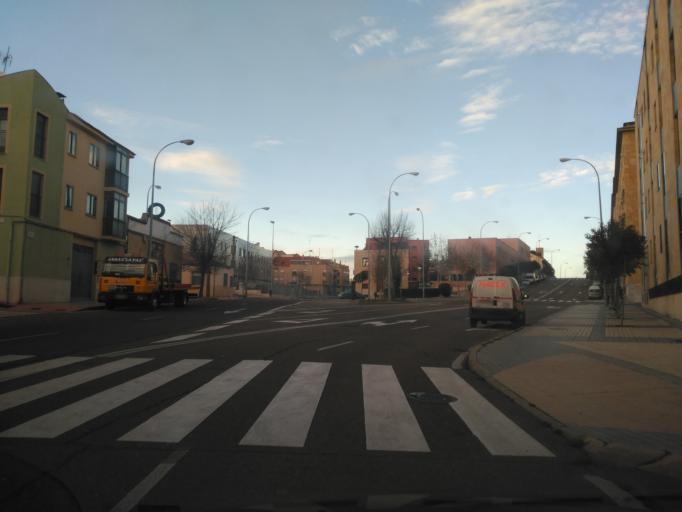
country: ES
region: Castille and Leon
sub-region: Provincia de Salamanca
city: Salamanca
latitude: 40.9783
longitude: -5.6679
